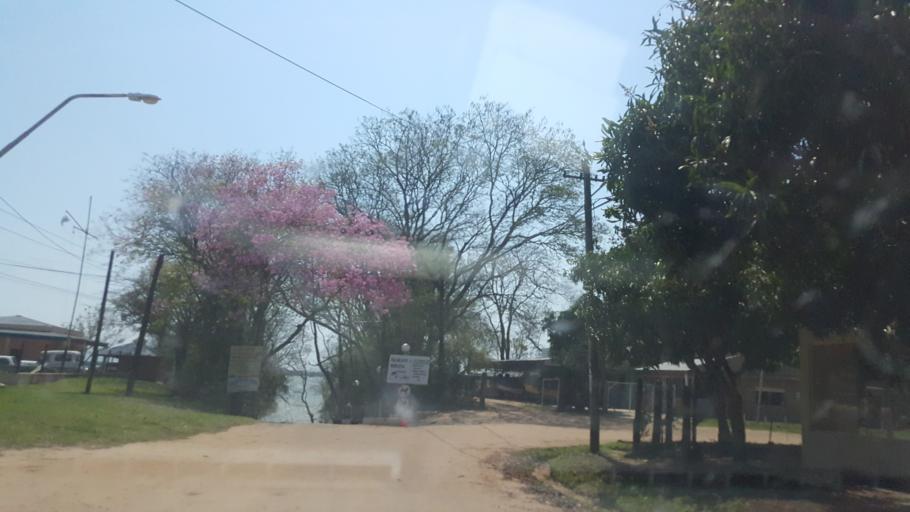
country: AR
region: Corrientes
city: Ita Ibate
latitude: -27.4236
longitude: -57.3330
